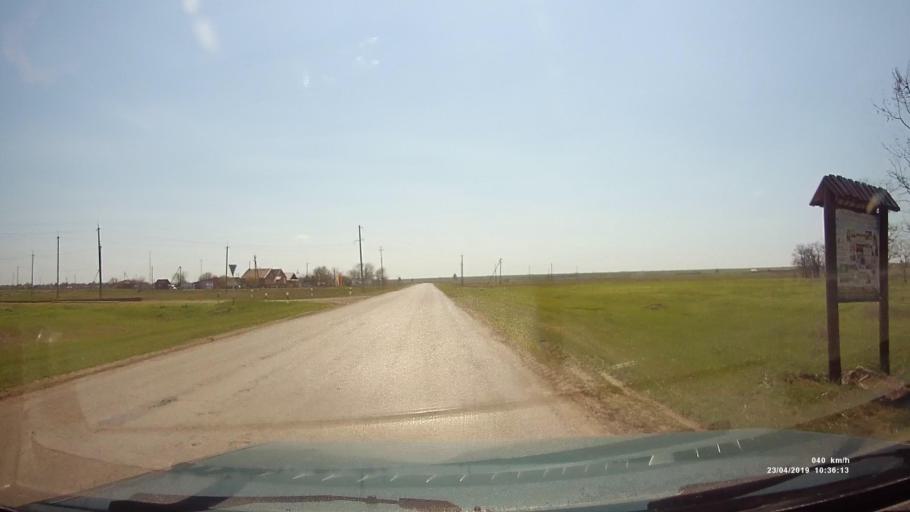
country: RU
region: Kalmykiya
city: Yashalta
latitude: 46.5468
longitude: 42.6334
